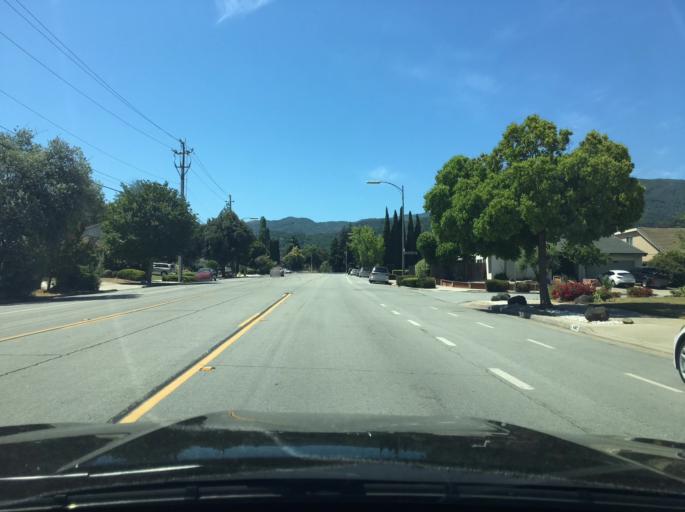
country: US
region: California
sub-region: Santa Clara County
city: Cambrian Park
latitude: 37.2240
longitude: -121.8765
